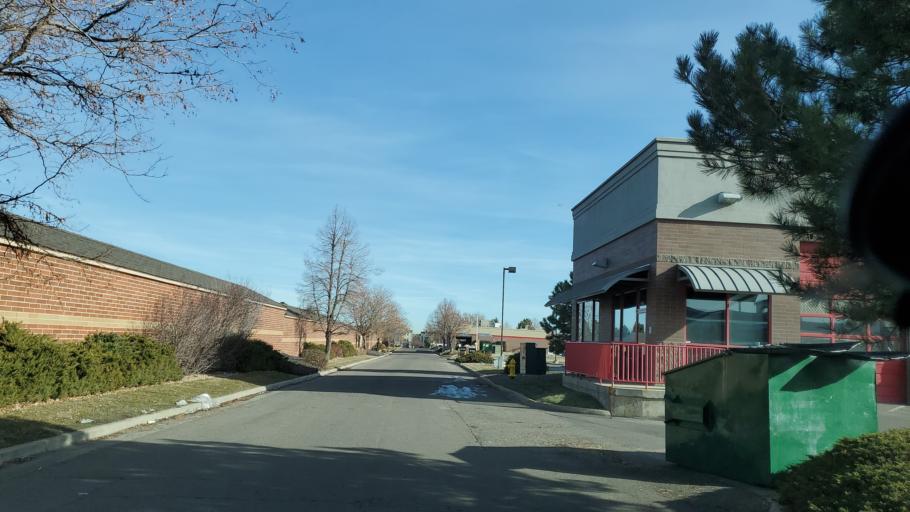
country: US
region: Colorado
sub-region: Adams County
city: Northglenn
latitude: 39.9149
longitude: -104.9561
